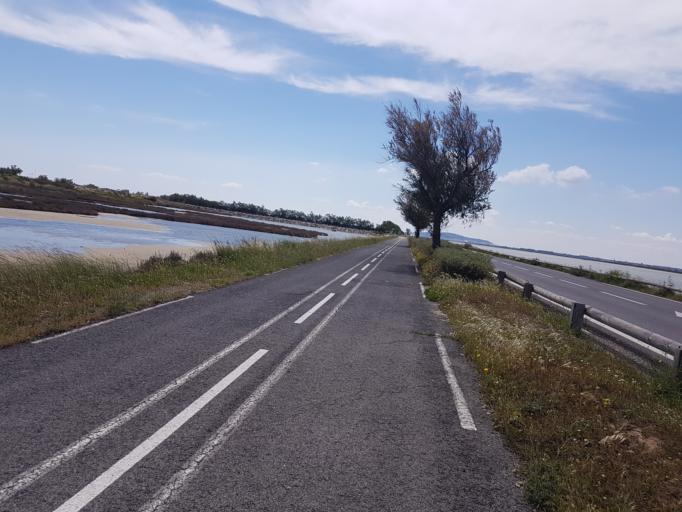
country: FR
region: Languedoc-Roussillon
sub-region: Departement de l'Herault
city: Vic-la-Gardiole
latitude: 43.4565
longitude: 3.8134
